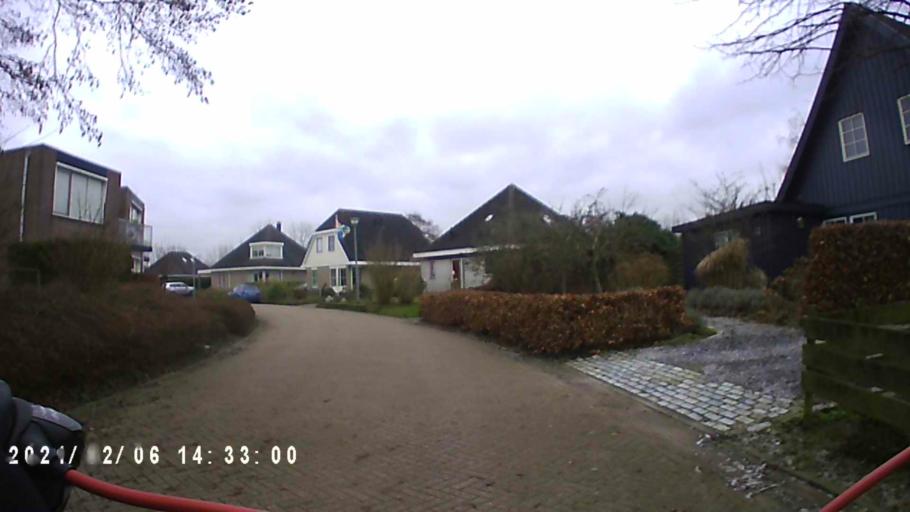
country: NL
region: Groningen
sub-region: Gemeente Winsum
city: Winsum
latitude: 53.3911
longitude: 6.5506
